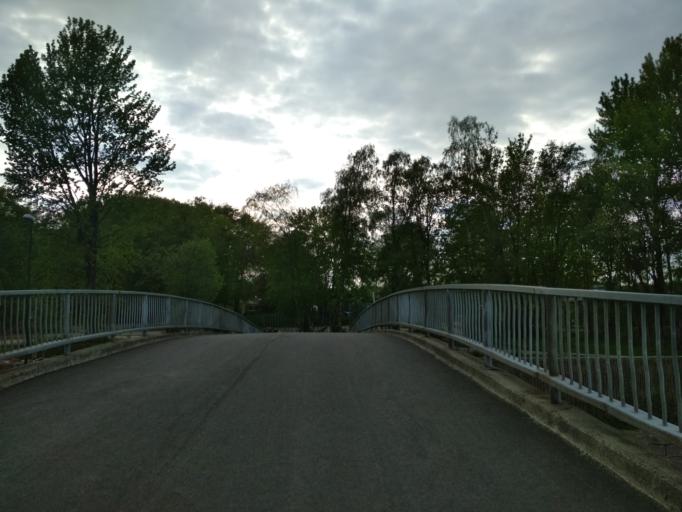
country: NO
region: Rogaland
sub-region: Stavanger
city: Stavanger
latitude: 58.9589
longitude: 5.7226
